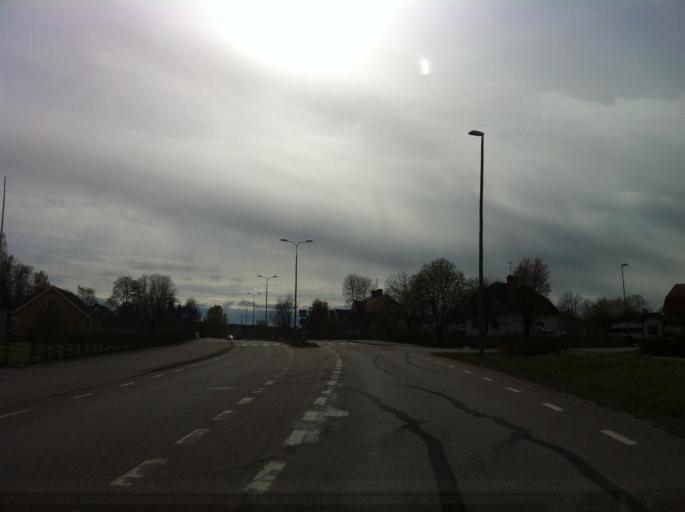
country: SE
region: Soedermanland
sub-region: Nykopings Kommun
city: Stigtomta
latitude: 58.7462
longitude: 16.7299
